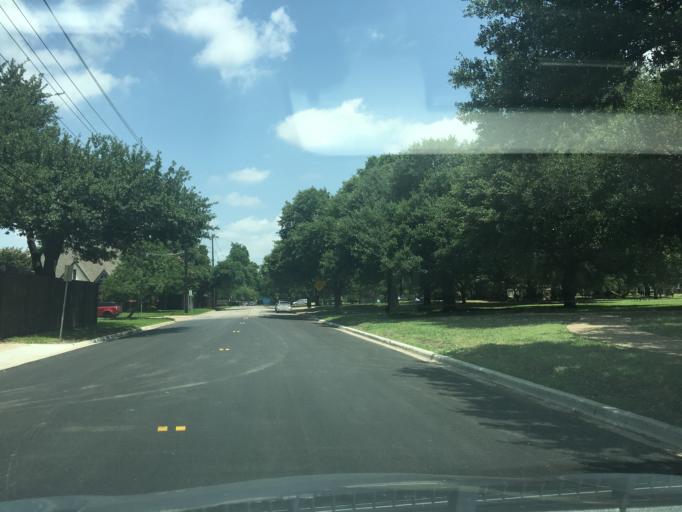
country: US
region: Texas
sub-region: Dallas County
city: University Park
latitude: 32.8719
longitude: -96.7915
